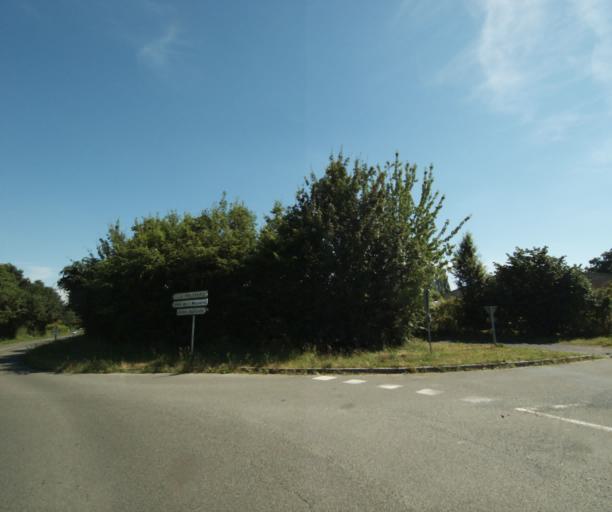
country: FR
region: Pays de la Loire
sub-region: Departement de la Mayenne
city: Laval
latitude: 48.0501
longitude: -0.7892
